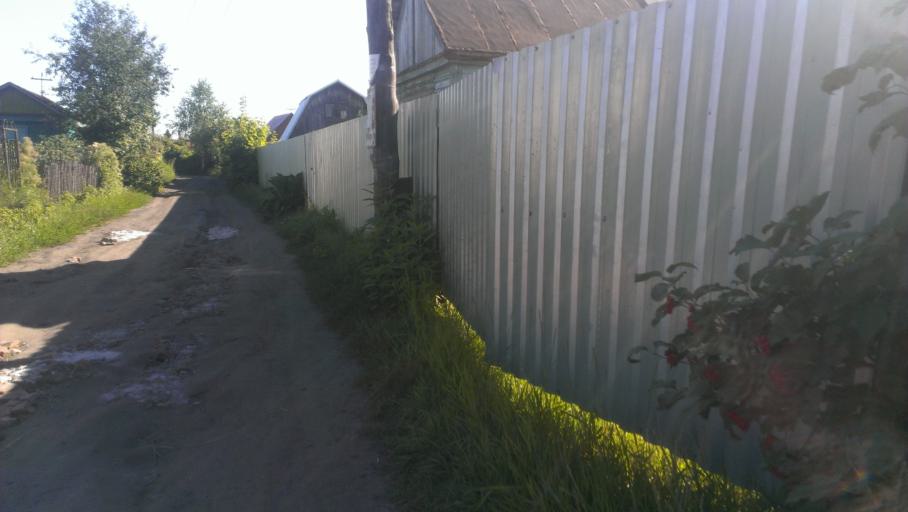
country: RU
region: Altai Krai
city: Novosilikatnyy
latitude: 53.3238
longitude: 83.6695
